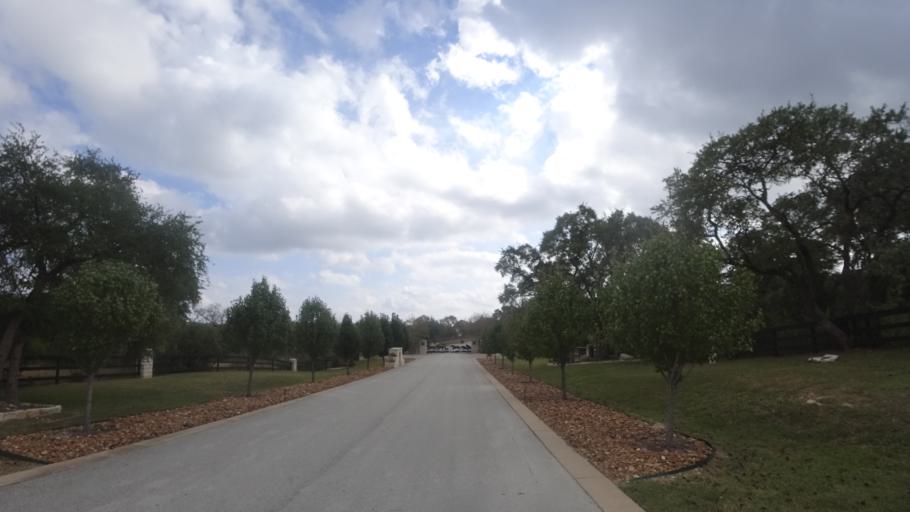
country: US
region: Texas
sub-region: Travis County
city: Barton Creek
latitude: 30.3104
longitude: -97.8865
